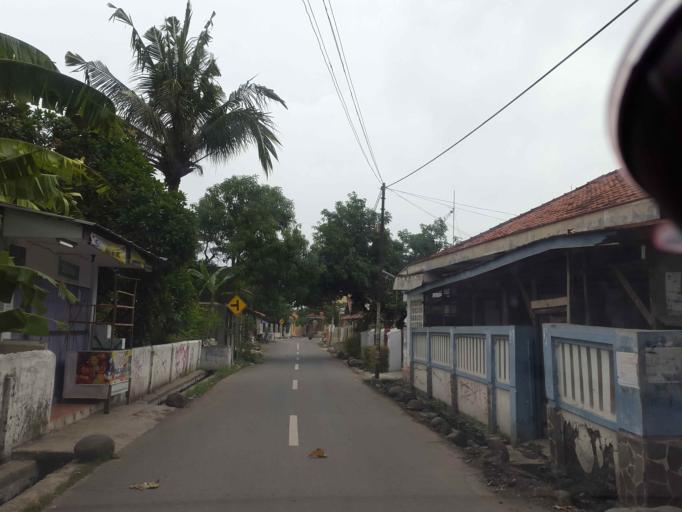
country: ID
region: Central Java
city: Dukuhturi
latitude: -6.8803
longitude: 109.0897
